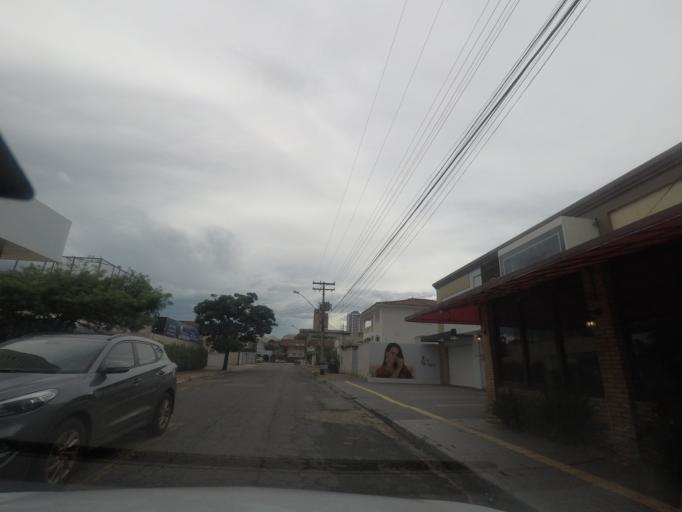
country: BR
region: Goias
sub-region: Goiania
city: Goiania
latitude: -16.6930
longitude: -49.2674
